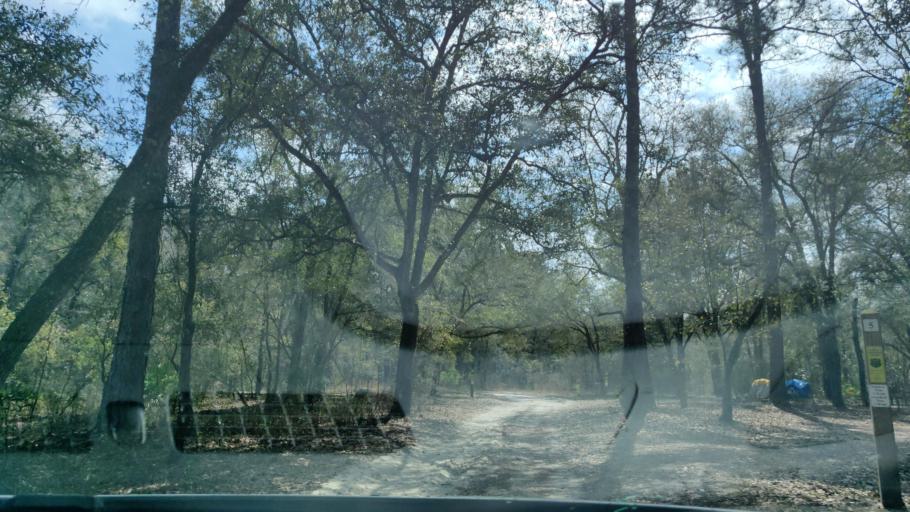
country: US
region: Florida
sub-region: Clay County
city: Middleburg
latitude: 30.1510
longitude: -81.9267
